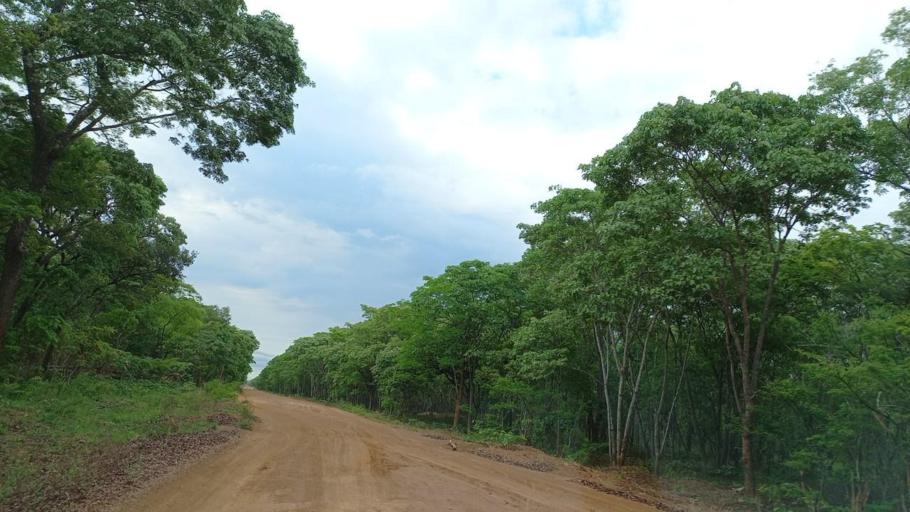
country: ZM
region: North-Western
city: Kalengwa
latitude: -13.3648
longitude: 25.0751
